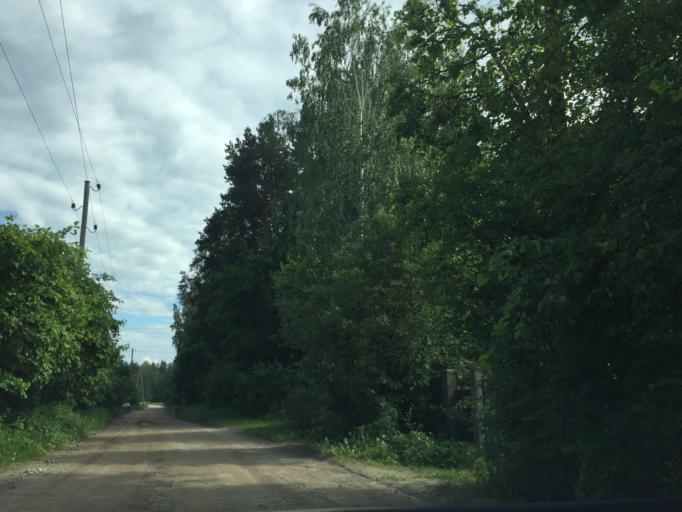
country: LV
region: Stopini
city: Ulbroka
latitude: 56.9278
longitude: 24.2901
